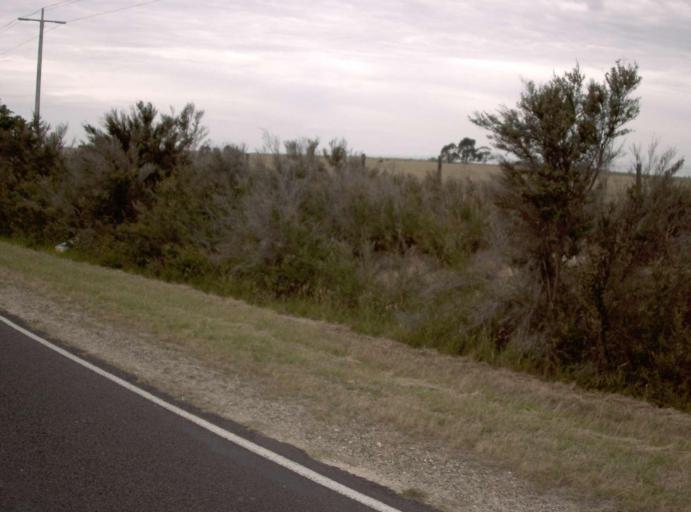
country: AU
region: Victoria
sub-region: Wellington
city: Sale
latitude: -38.1790
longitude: 147.2271
